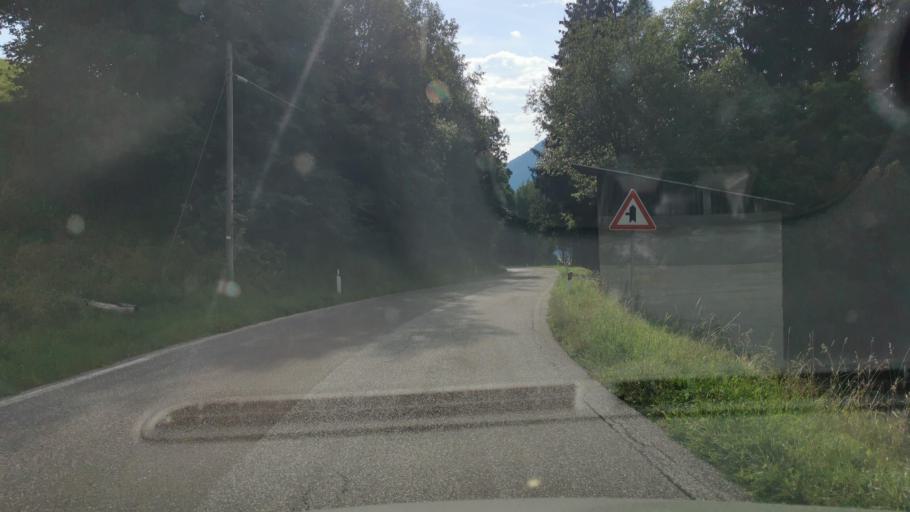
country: IT
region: Trentino-Alto Adige
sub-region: Provincia di Trento
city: Fierozzo
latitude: 46.1132
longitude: 11.3231
